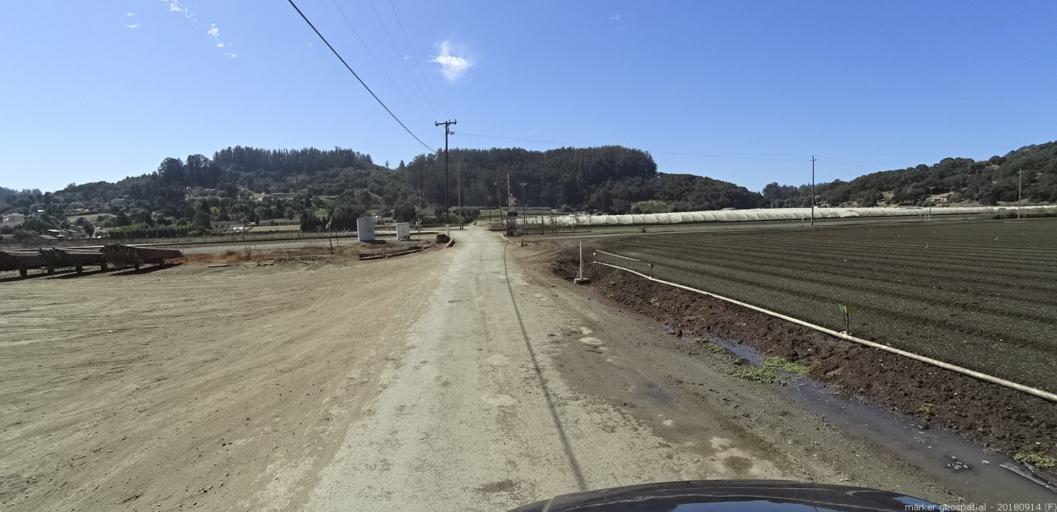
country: US
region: California
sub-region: San Benito County
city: Aromas
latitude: 36.8919
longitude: -121.6508
